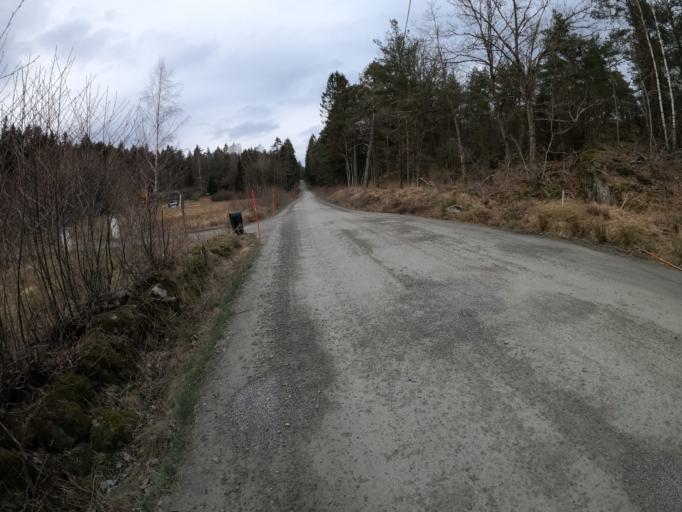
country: SE
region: Vaestra Goetaland
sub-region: Harryda Kommun
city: Molnlycke
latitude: 57.6352
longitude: 12.1011
